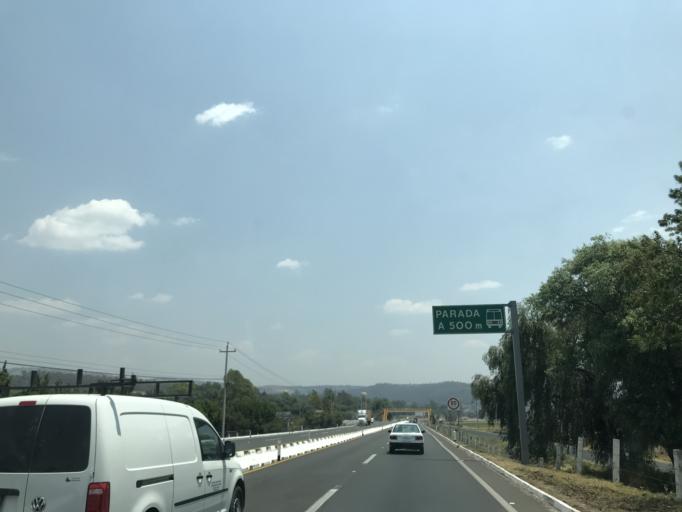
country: MX
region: Tlaxcala
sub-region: Ixtacuixtla de Mariano Matamoros
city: Villa Mariano Matamoros
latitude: 19.3235
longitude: -98.3696
